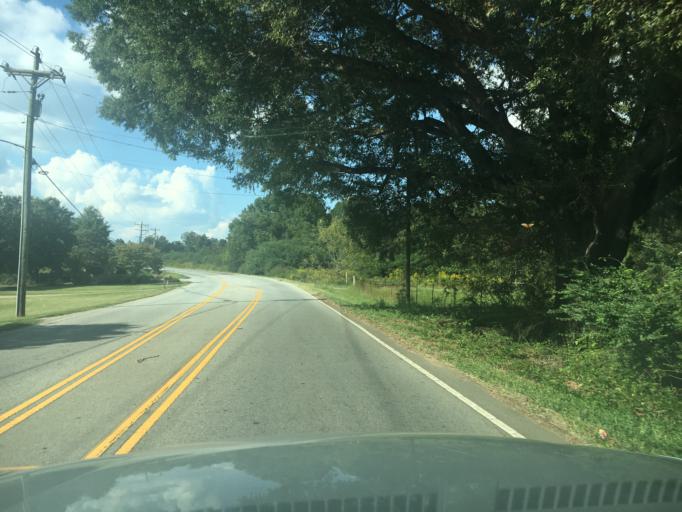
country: US
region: South Carolina
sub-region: Greenville County
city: Simpsonville
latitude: 34.6934
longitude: -82.2529
